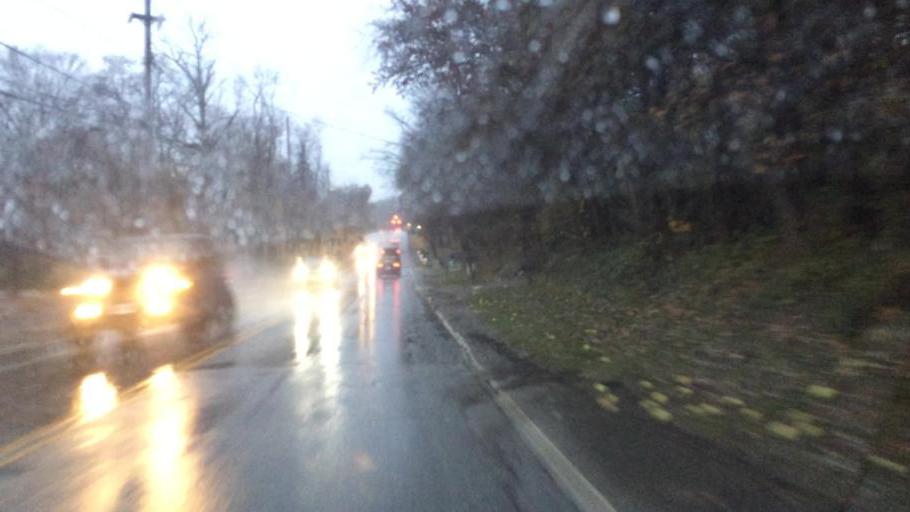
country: US
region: Ohio
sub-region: Cuyahoga County
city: Olmsted Falls
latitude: 41.3874
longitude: -81.9030
